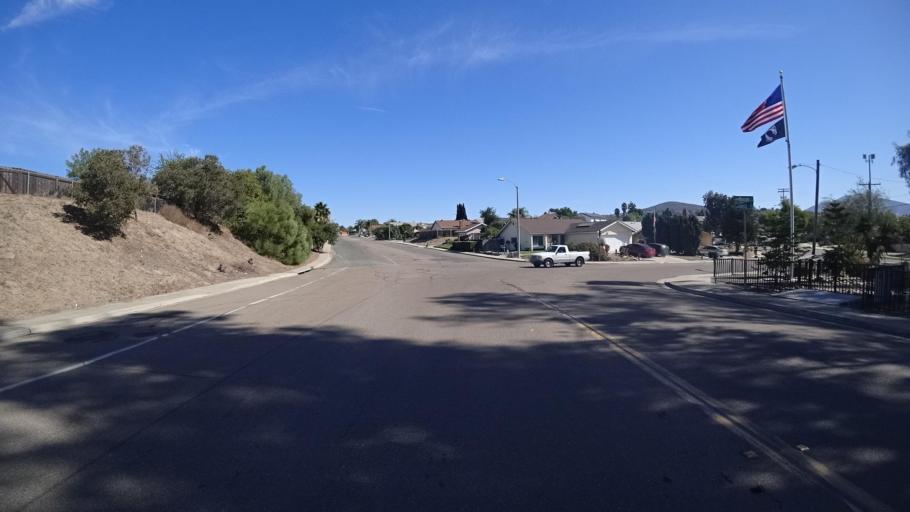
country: US
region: California
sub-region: San Diego County
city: Lemon Grove
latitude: 32.7252
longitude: -117.0210
